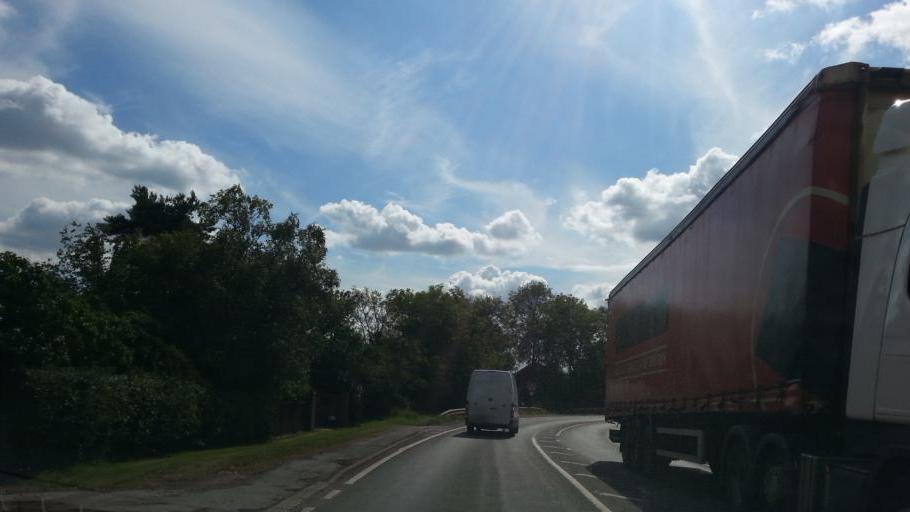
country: GB
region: England
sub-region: Nottinghamshire
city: Newark on Trent
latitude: 53.1089
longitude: -0.8200
